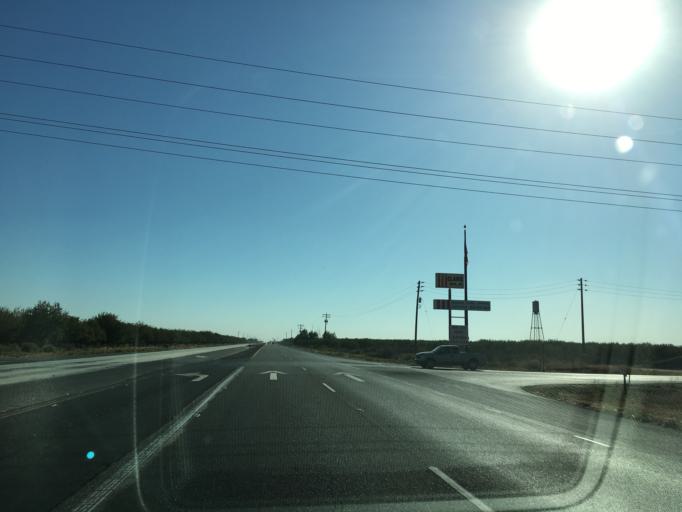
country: US
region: California
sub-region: Merced County
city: Dos Palos
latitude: 37.0835
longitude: -120.4744
